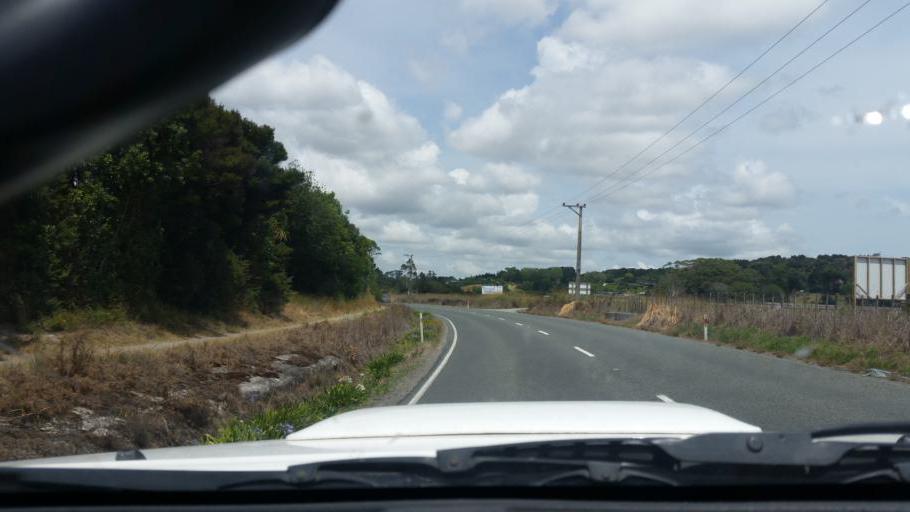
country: NZ
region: Auckland
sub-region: Auckland
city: Wellsford
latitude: -36.1115
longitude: 174.5759
